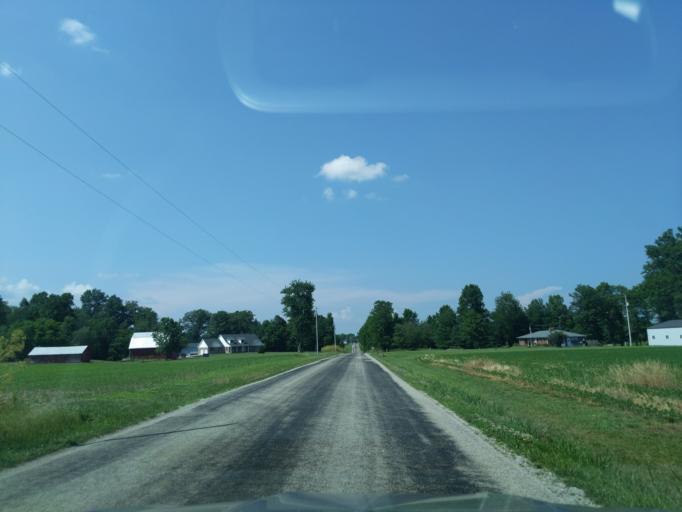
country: US
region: Indiana
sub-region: Ripley County
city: Osgood
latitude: 39.0806
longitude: -85.3480
